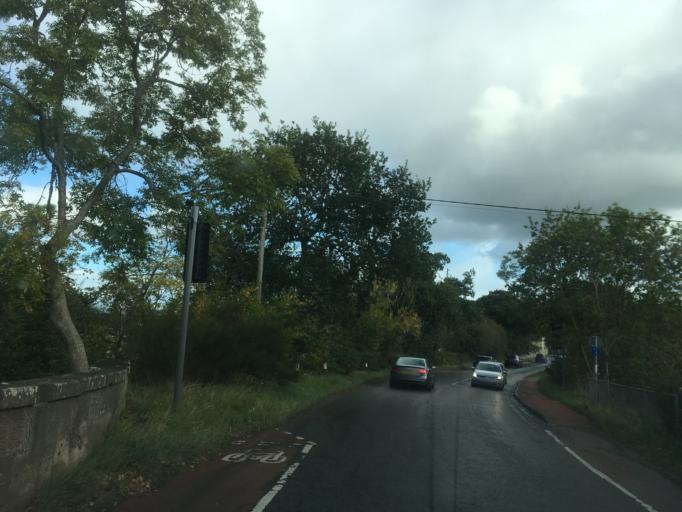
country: GB
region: Scotland
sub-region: Highland
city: Beauly
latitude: 57.4706
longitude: -4.4754
